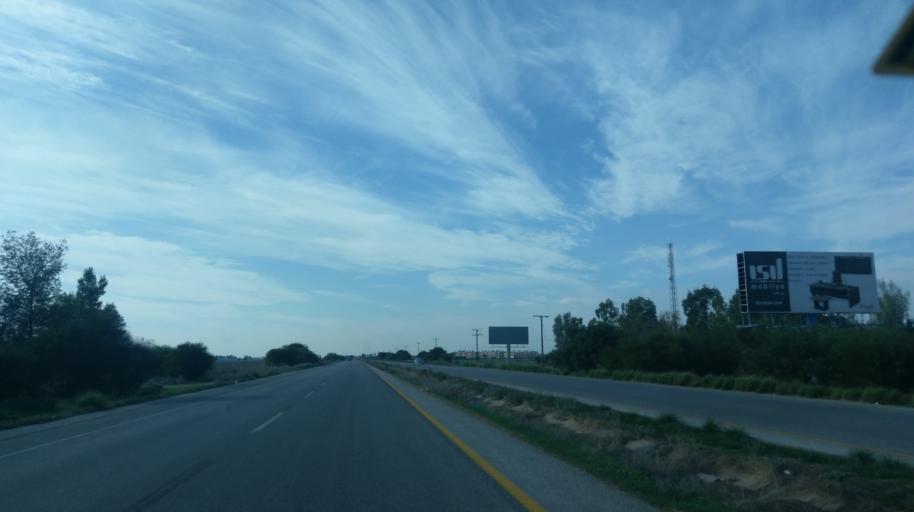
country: CY
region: Ammochostos
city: Lefkonoiko
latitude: 35.1860
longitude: 33.6534
